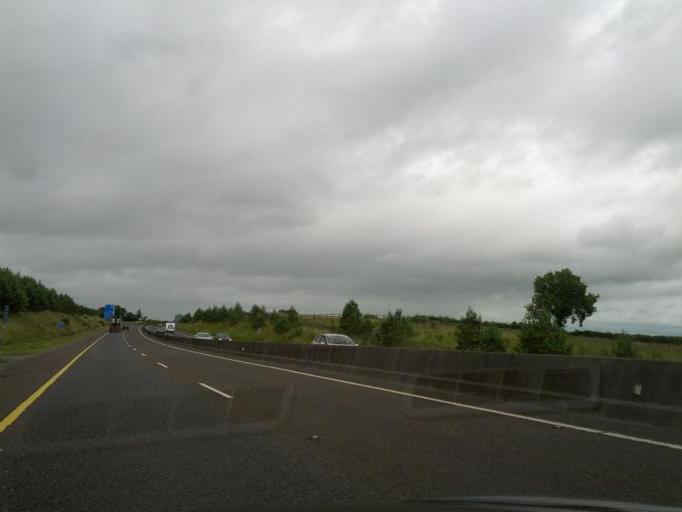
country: IE
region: Munster
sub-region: An Clar
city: Ennis
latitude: 52.8147
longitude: -8.9358
